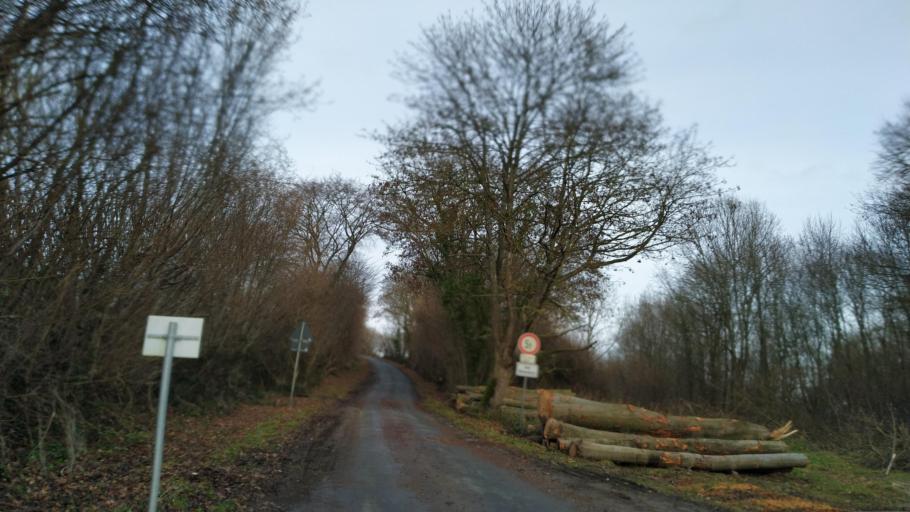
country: DE
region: Schleswig-Holstein
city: Malente
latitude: 54.1985
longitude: 10.5969
